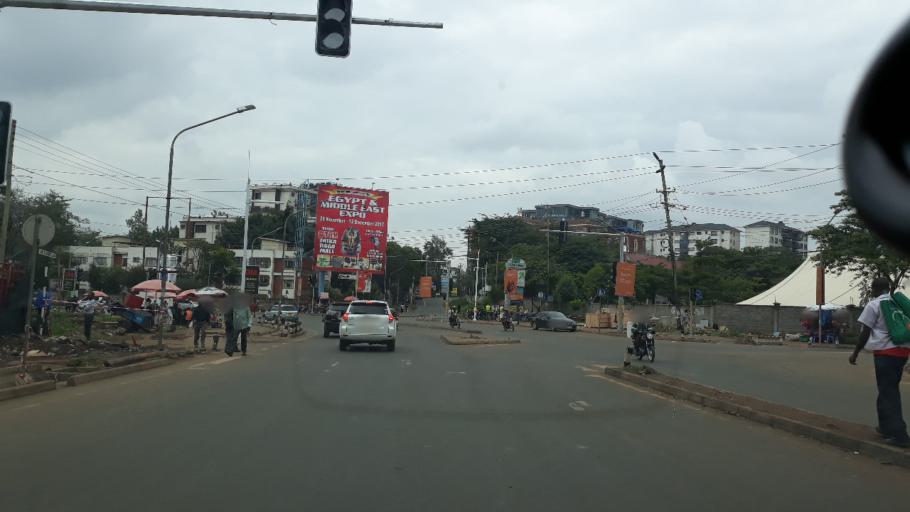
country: KE
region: Nairobi Area
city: Nairobi
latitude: -1.2653
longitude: 36.8013
